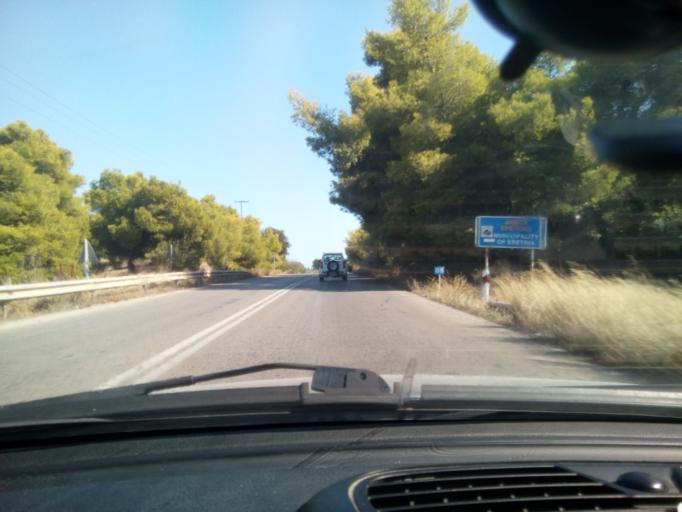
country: GR
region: Central Greece
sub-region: Nomos Evvoias
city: Malakonta
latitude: 38.4104
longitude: 23.7249
